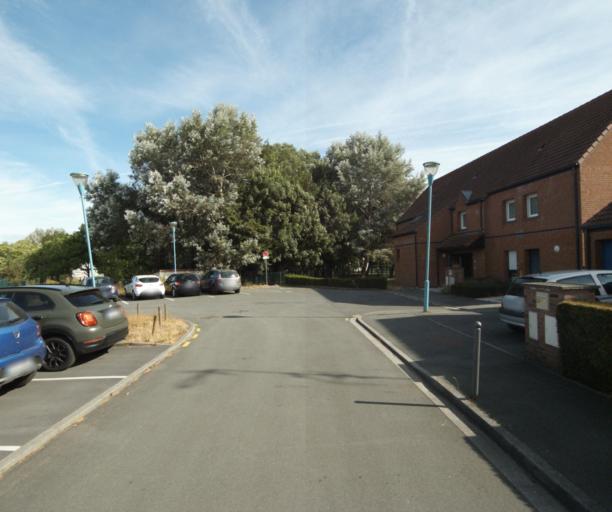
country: FR
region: Nord-Pas-de-Calais
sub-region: Departement du Nord
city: Linselles
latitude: 50.7369
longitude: 3.0879
